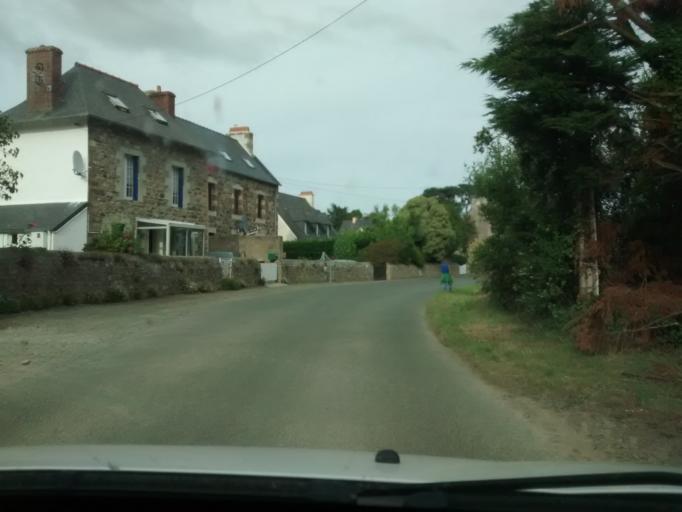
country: FR
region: Brittany
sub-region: Departement des Cotes-d'Armor
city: Plougrescant
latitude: 48.8473
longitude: -3.2410
